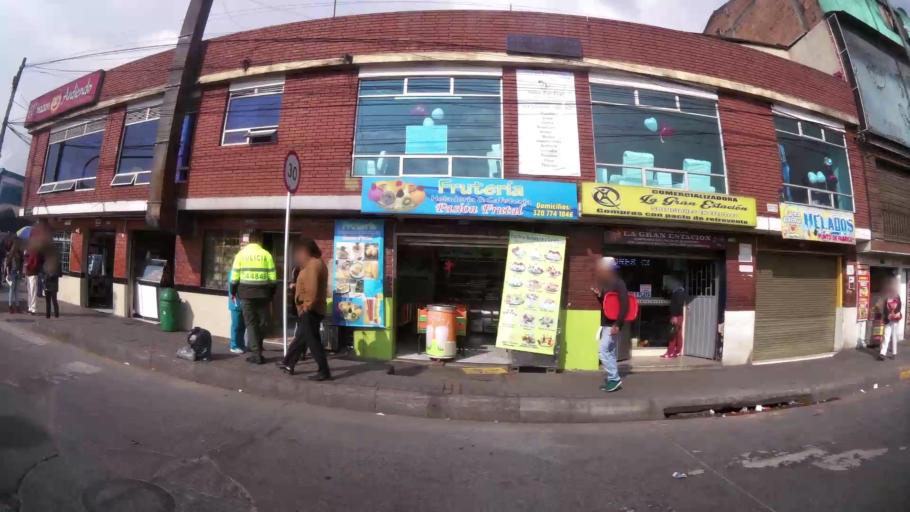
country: CO
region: Bogota D.C.
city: Bogota
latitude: 4.5577
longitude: -74.1220
